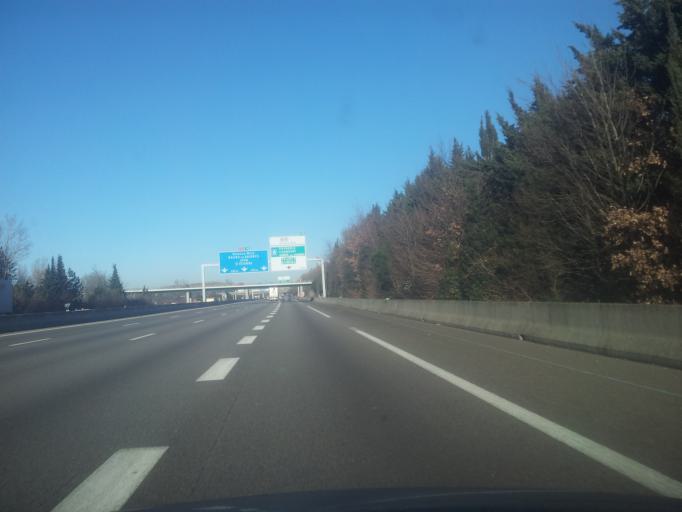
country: FR
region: Rhone-Alpes
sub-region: Departement de la Drome
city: Portes-les-Valence
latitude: 44.8998
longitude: 4.8754
